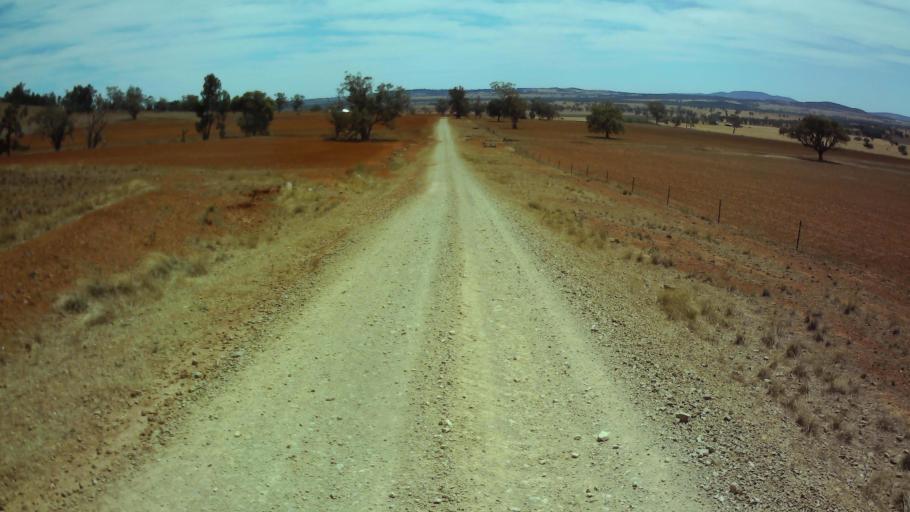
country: AU
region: New South Wales
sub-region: Weddin
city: Grenfell
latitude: -33.7484
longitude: 148.1654
